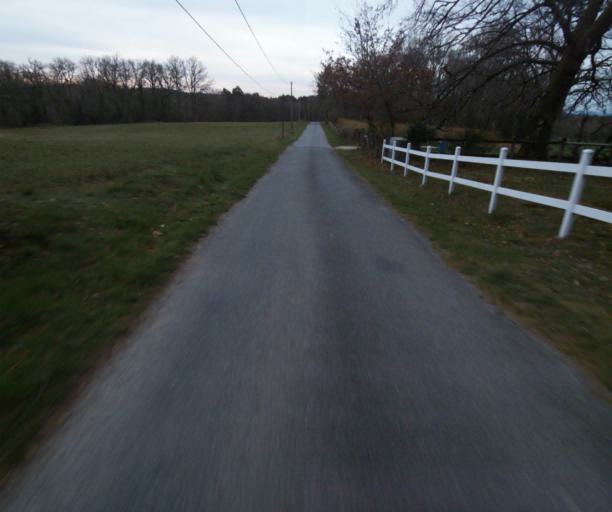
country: FR
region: Limousin
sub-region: Departement de la Correze
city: Correze
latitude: 45.4366
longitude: 1.8413
